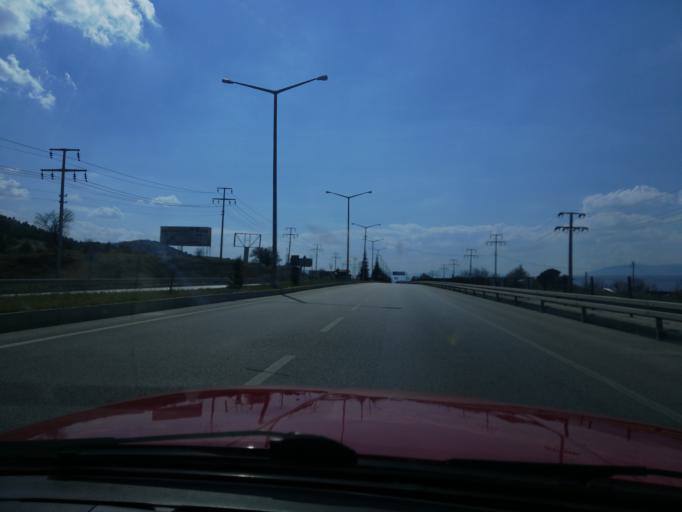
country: TR
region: Burdur
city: Burdur
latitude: 37.7504
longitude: 30.3290
